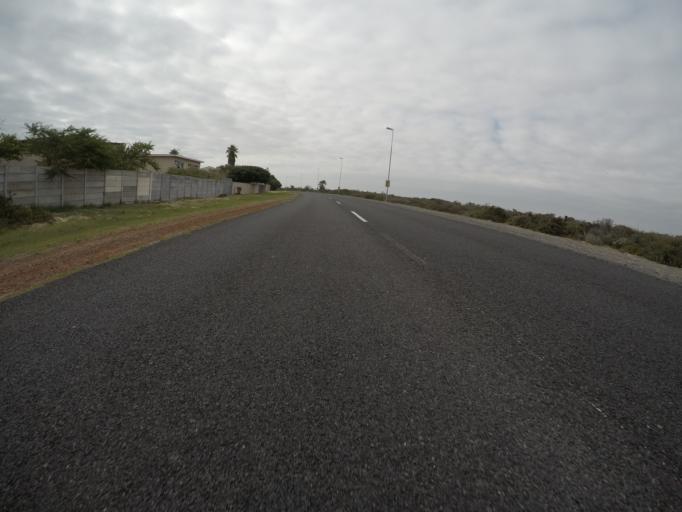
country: ZA
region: Western Cape
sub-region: City of Cape Town
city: Atlantis
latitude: -33.7091
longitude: 18.4471
